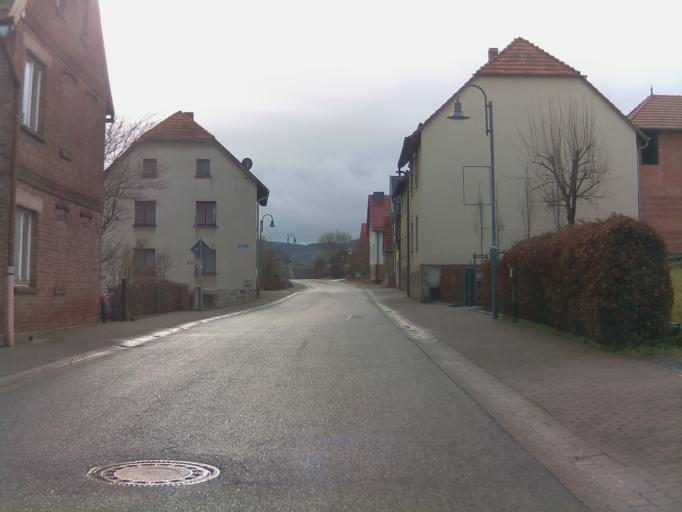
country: DE
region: Thuringia
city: Geisa
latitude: 50.6805
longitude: 9.9281
